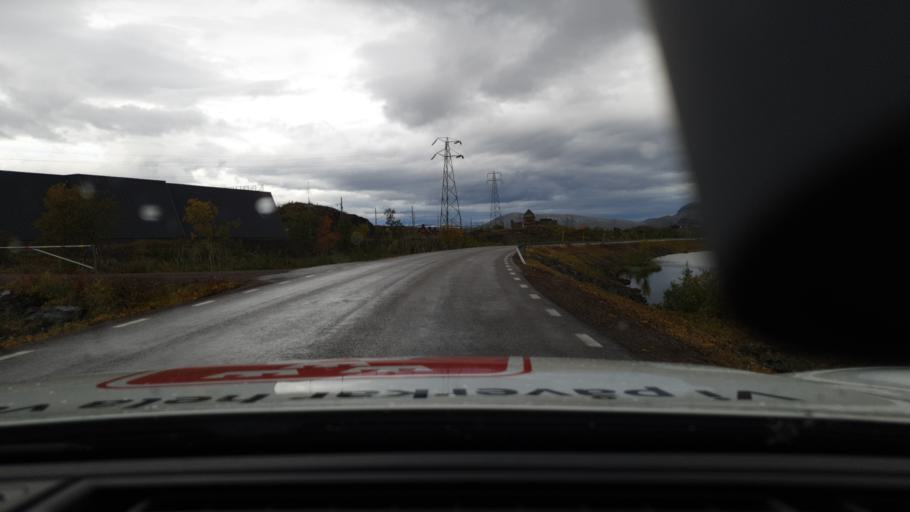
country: NO
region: Troms
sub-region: Bardu
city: Setermoen
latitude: 68.4278
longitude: 18.2750
